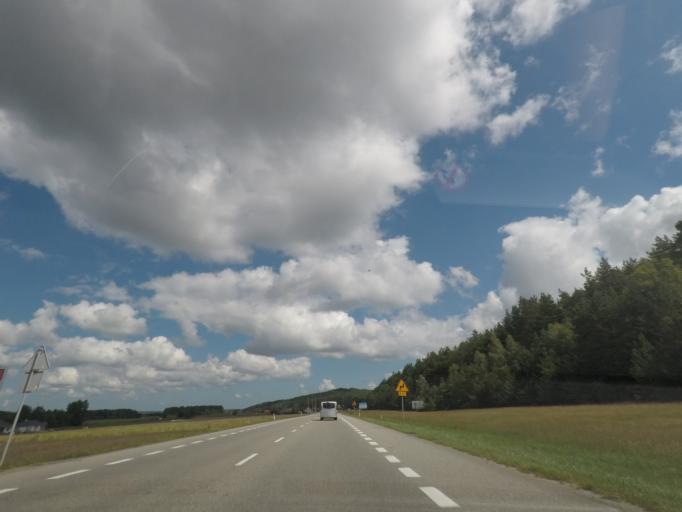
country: PL
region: Pomeranian Voivodeship
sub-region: Powiat wejherowski
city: Luzino
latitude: 54.5760
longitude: 18.0648
